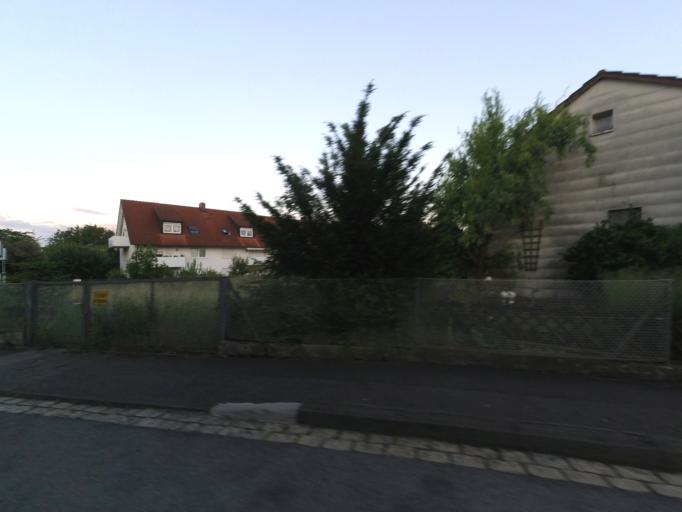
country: DE
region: Bavaria
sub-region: Regierungsbezirk Unterfranken
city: Hassfurt
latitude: 50.0330
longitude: 10.5163
